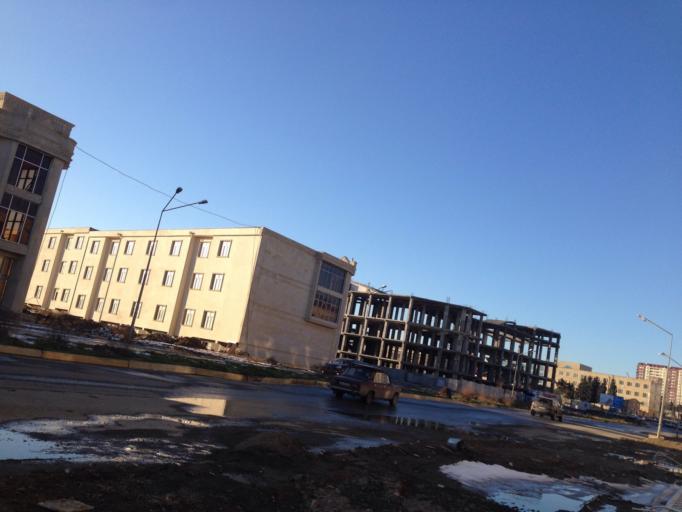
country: AZ
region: Baki
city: Baku
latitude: 40.4125
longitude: 49.8573
